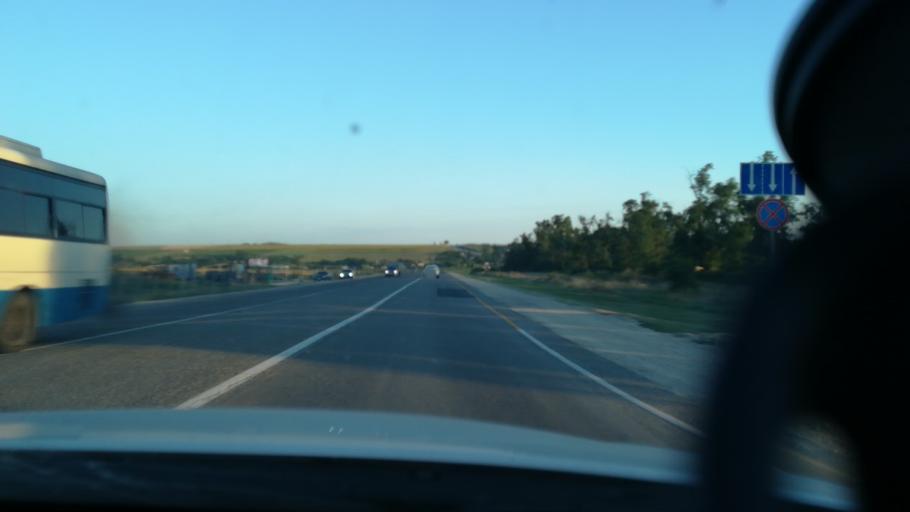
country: RU
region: Krasnodarskiy
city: Dzhiginka
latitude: 45.1018
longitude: 37.3174
